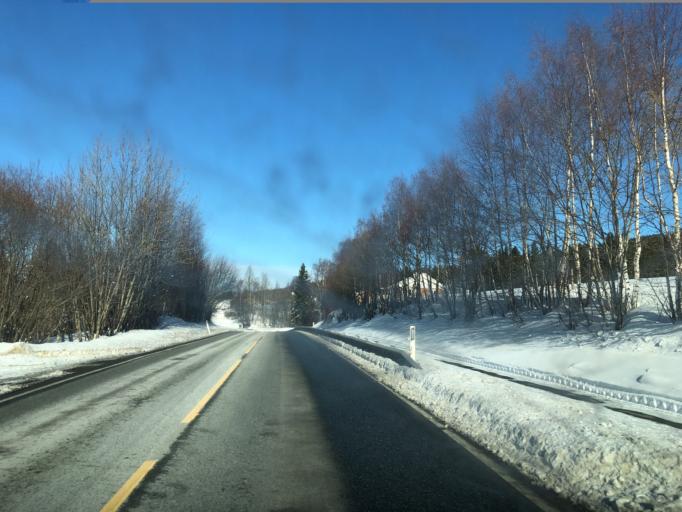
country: NO
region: Oppland
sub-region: Jevnaker
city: Jevnaker
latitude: 60.1876
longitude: 10.3625
